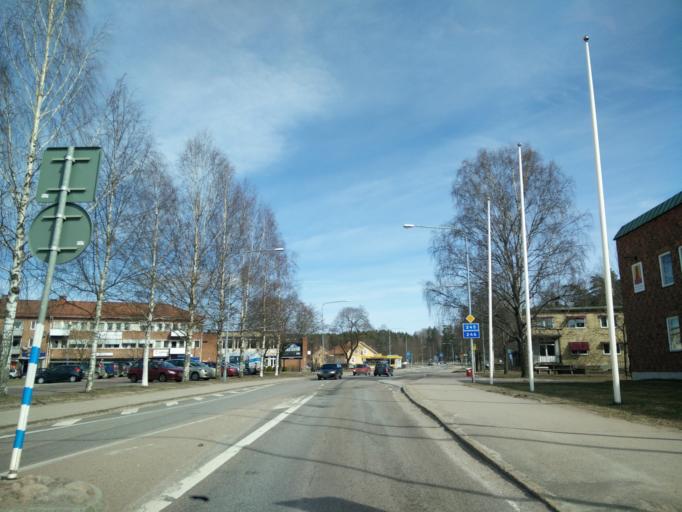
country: SE
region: Vaermland
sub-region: Hagfors Kommun
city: Hagfors
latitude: 60.0313
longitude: 13.7015
